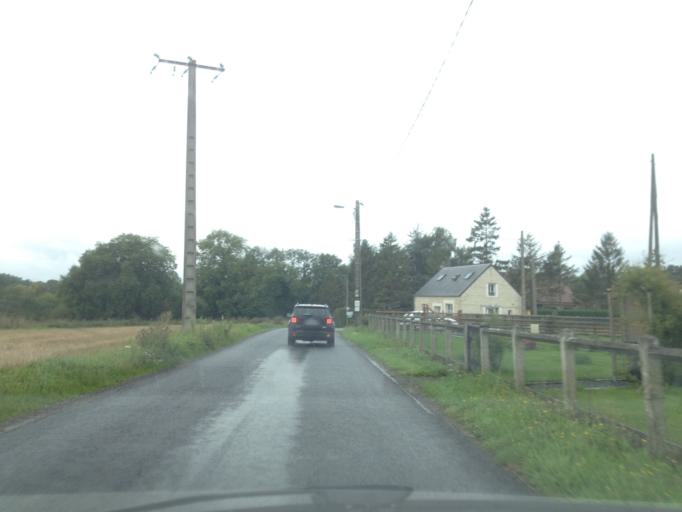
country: FR
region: Lower Normandy
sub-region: Departement du Calvados
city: Saint-Vigor-le-Grand
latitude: 49.3000
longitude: -0.6908
